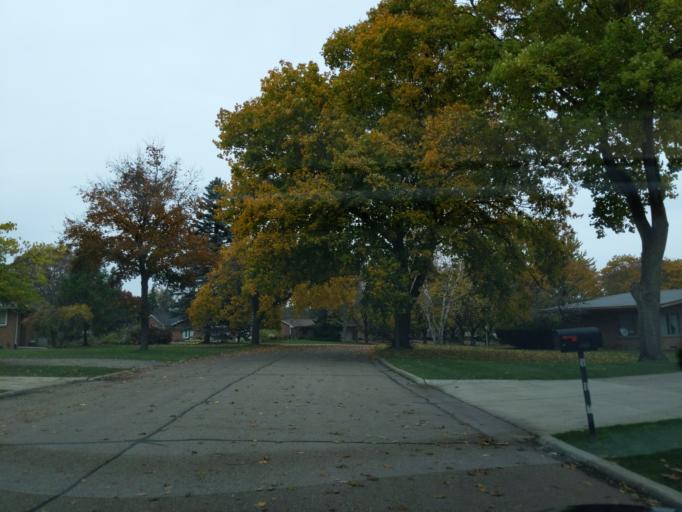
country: US
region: Michigan
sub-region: Ingham County
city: Edgemont Park
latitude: 42.7136
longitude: -84.5906
